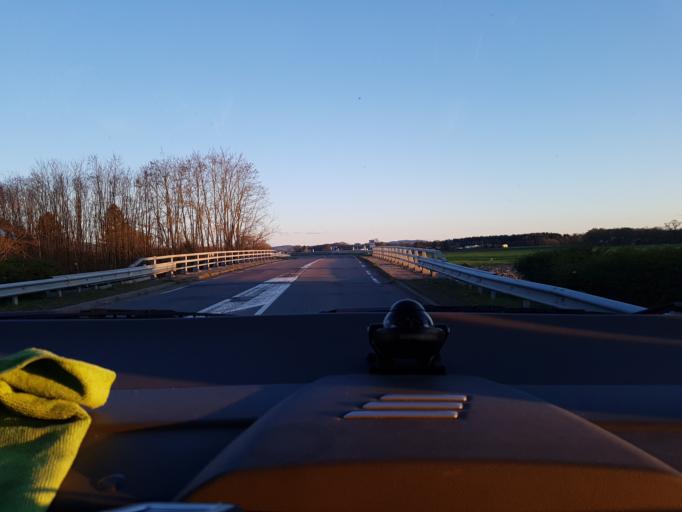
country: FR
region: Bourgogne
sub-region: Departement de Saone-et-Loire
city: Etang-sur-Arroux
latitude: 46.8692
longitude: 4.1756
